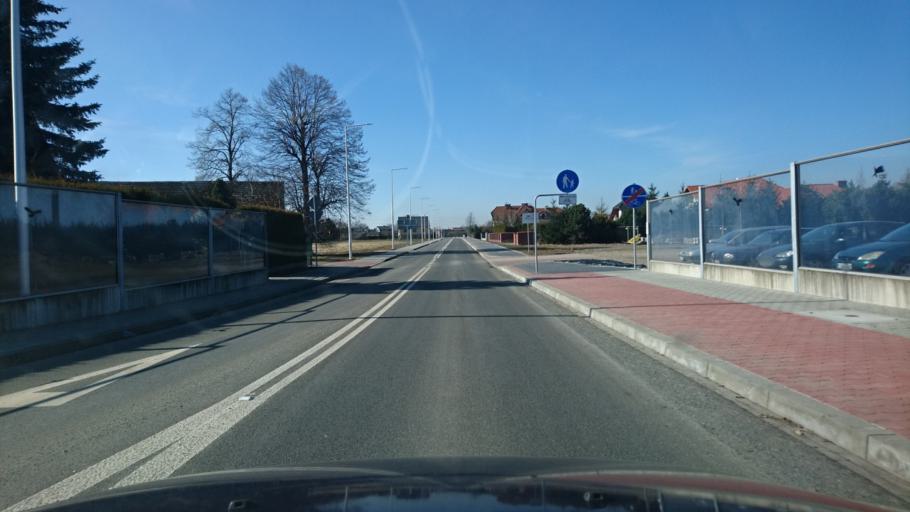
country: PL
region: Lesser Poland Voivodeship
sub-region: Powiat oswiecimski
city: Kety
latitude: 49.8915
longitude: 19.2189
